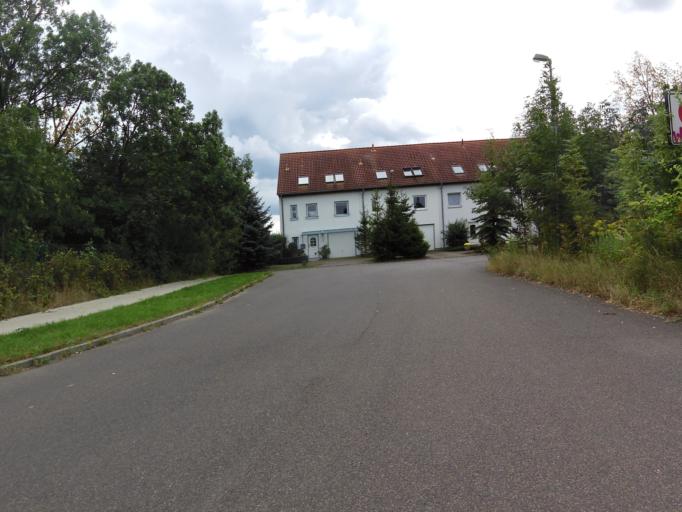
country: DE
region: Saxony
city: Leipzig
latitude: 51.3874
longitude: 12.3618
